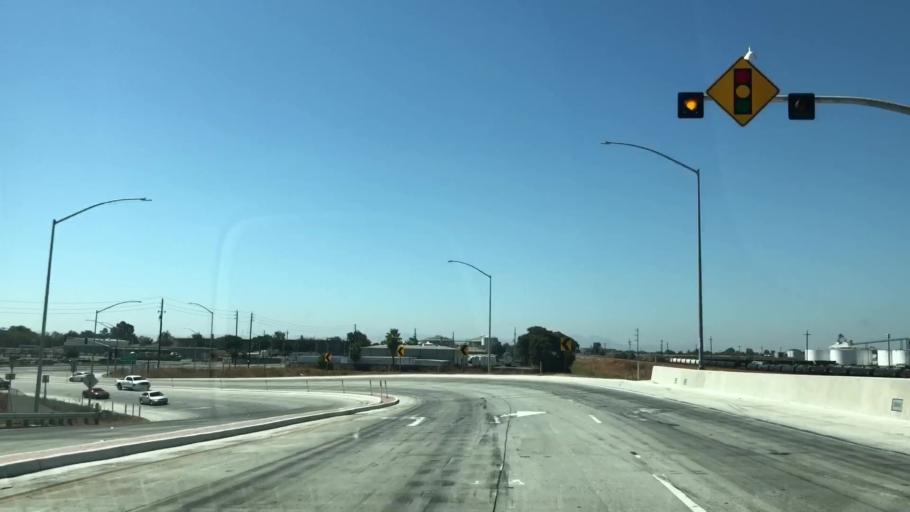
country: US
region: California
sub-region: San Joaquin County
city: Country Club
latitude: 37.9387
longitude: -121.3215
